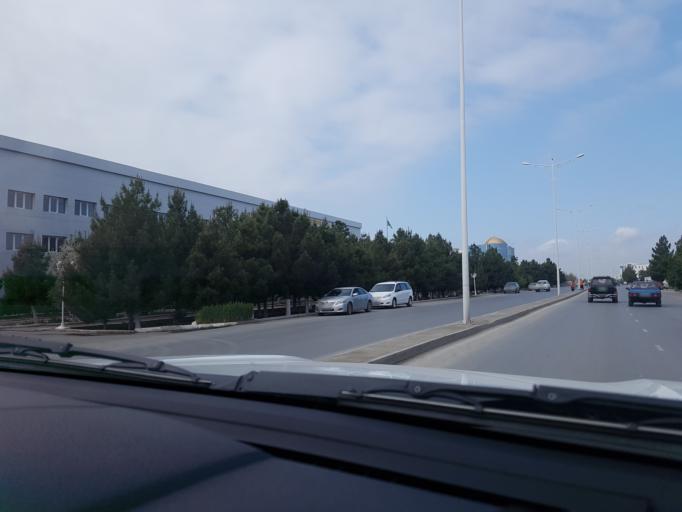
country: TM
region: Lebap
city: Turkmenabat
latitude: 39.0725
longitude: 63.5913
